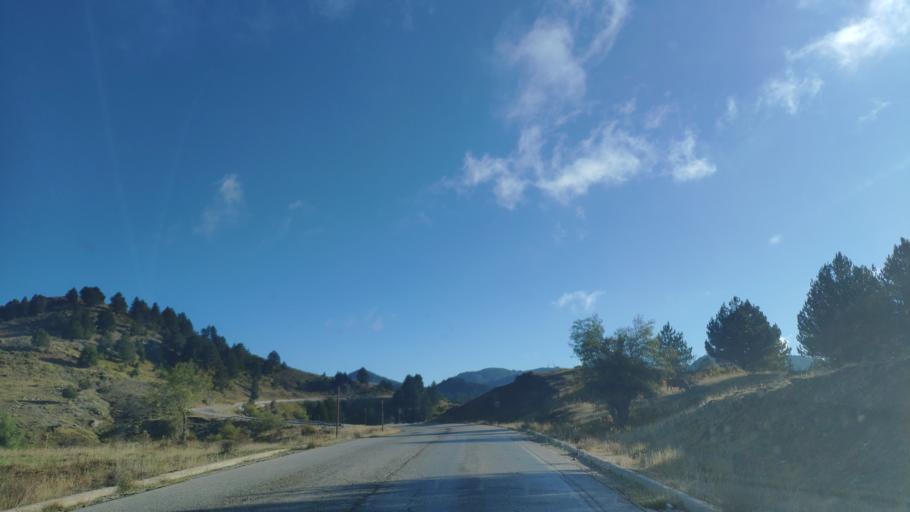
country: GR
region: Epirus
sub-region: Nomos Ioanninon
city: Metsovo
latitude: 39.7945
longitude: 21.1668
